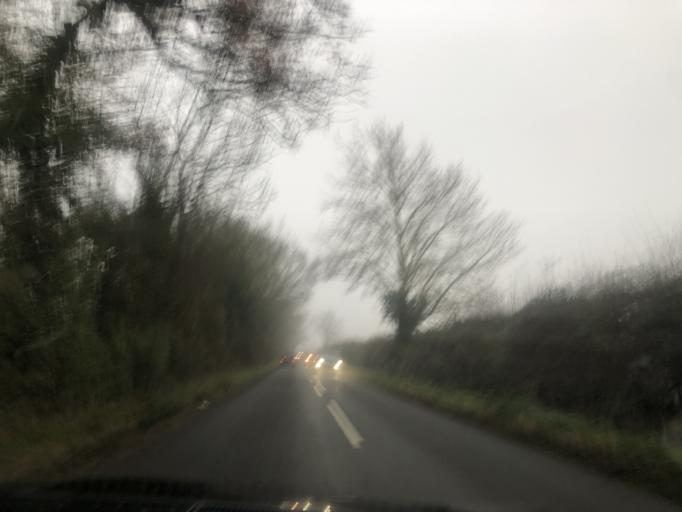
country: GB
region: England
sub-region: Oxfordshire
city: Bicester
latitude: 51.9217
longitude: -1.1842
